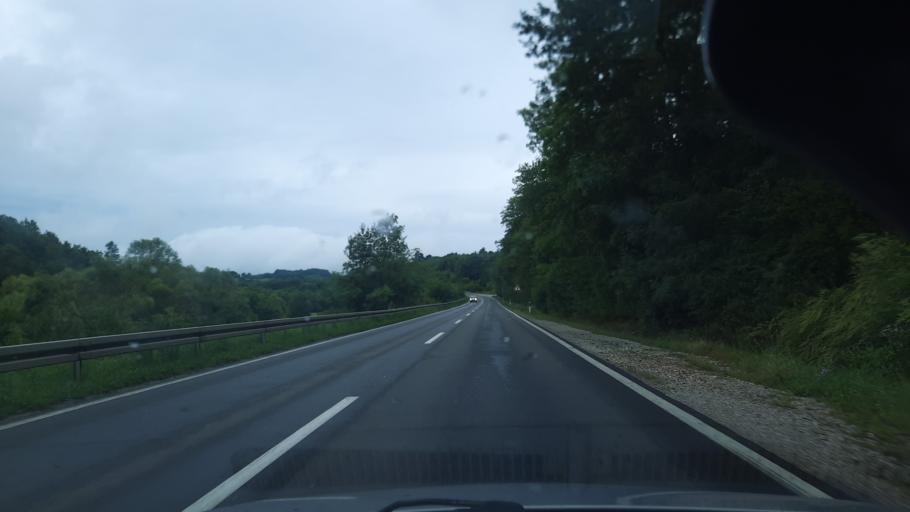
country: RS
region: Central Serbia
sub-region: Sumadijski Okrug
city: Knic
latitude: 43.9567
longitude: 20.8057
